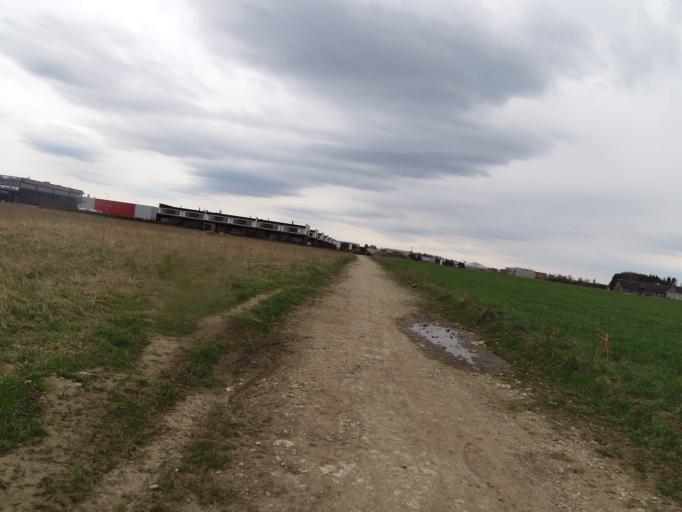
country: EE
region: Harju
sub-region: Tallinna linn
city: Tallinn
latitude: 59.3916
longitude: 24.8184
